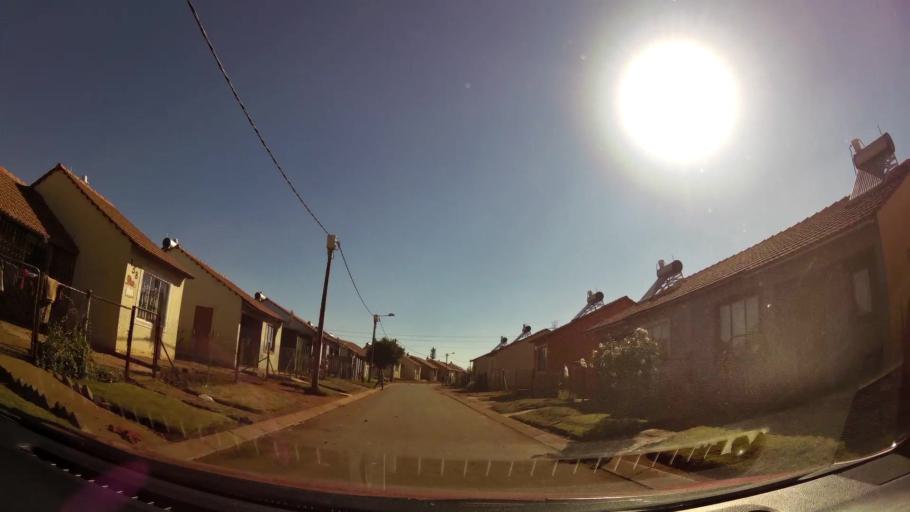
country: ZA
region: Gauteng
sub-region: City of Johannesburg Metropolitan Municipality
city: Soweto
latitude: -26.2354
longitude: 27.7976
